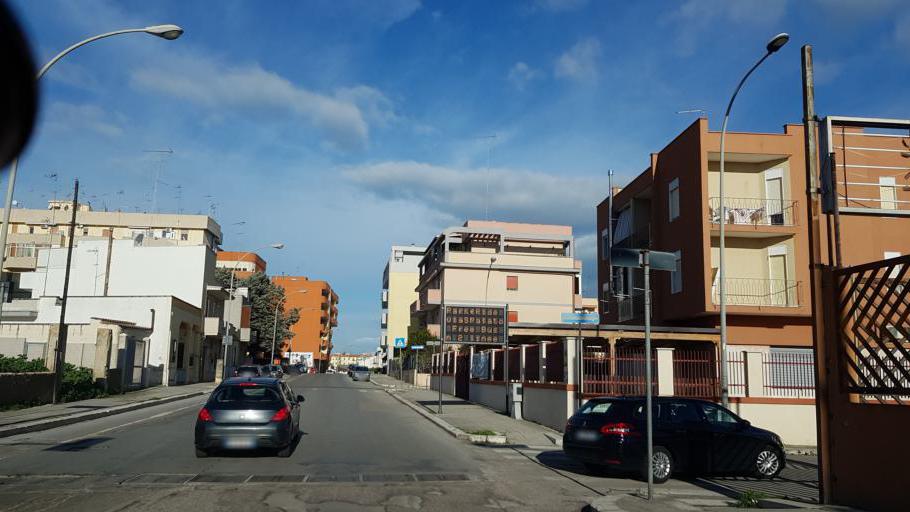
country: IT
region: Apulia
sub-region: Provincia di Brindisi
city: Brindisi
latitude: 40.6206
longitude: 17.9335
